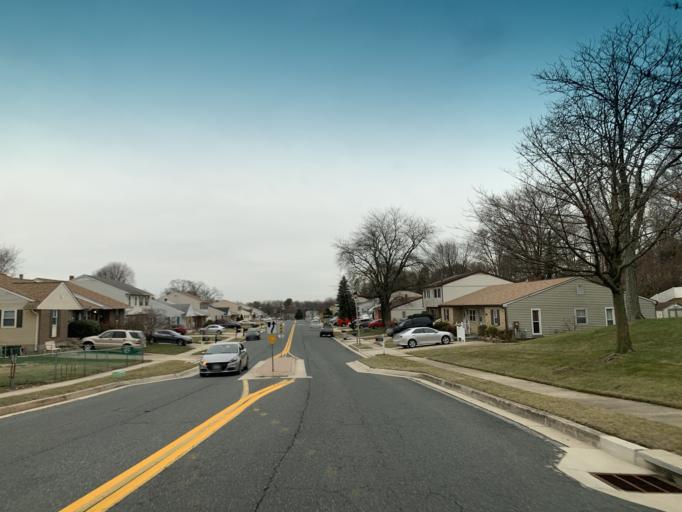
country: US
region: Maryland
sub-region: Baltimore County
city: Carney
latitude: 39.3893
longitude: -76.4898
